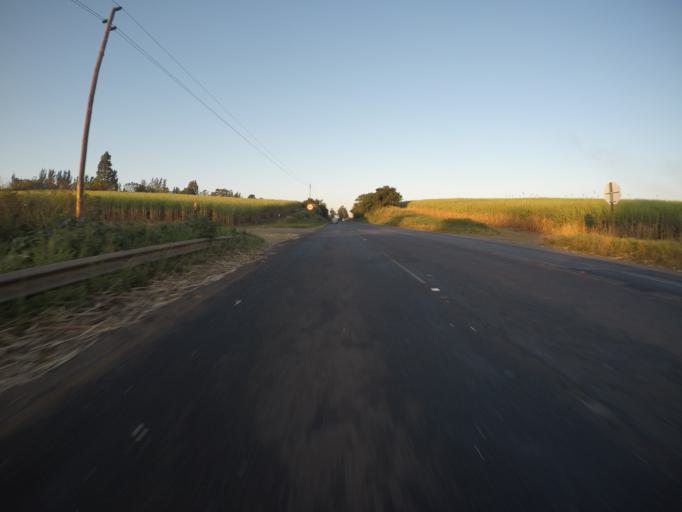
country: ZA
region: KwaZulu-Natal
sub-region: uThungulu District Municipality
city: Empangeni
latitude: -28.7958
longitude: 31.8966
